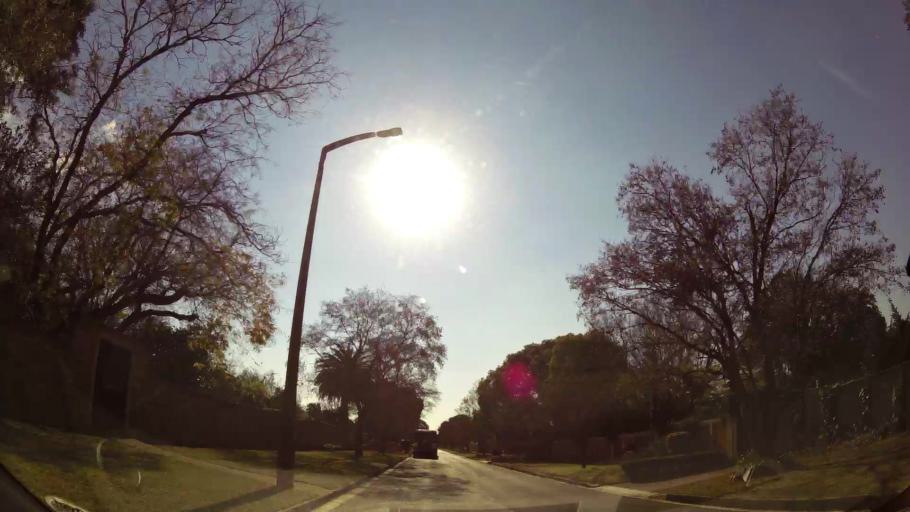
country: ZA
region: Gauteng
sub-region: Ekurhuleni Metropolitan Municipality
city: Benoni
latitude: -26.1434
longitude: 28.3429
